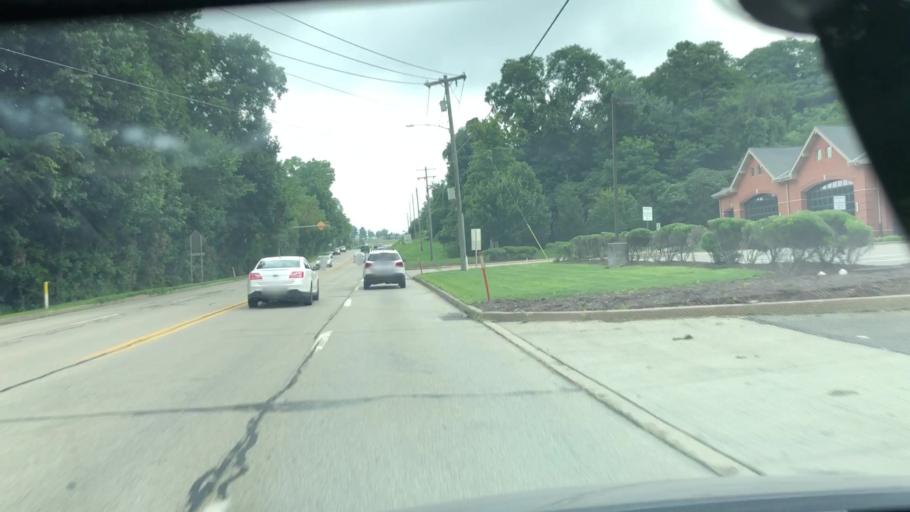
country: US
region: Pennsylvania
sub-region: Allegheny County
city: Mount Lebanon
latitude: 40.3407
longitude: -80.0636
